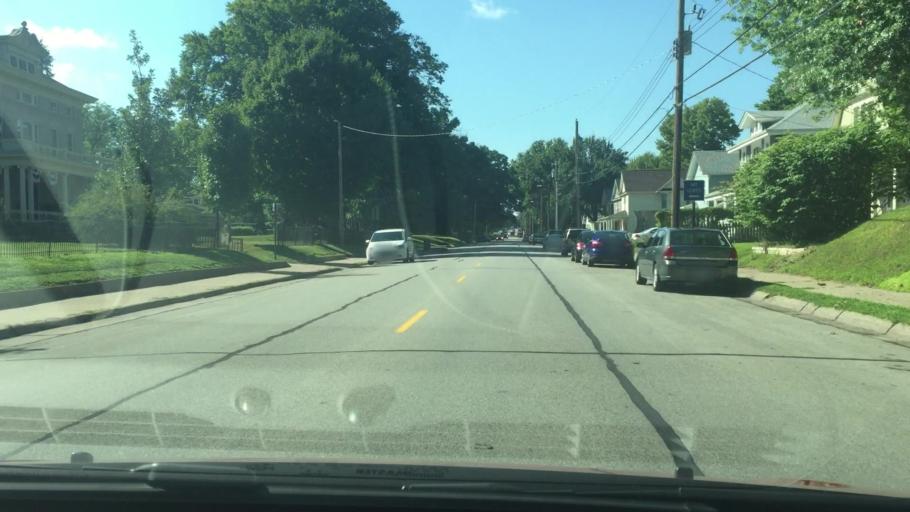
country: US
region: Iowa
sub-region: Muscatine County
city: Muscatine
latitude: 41.4324
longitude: -91.0506
